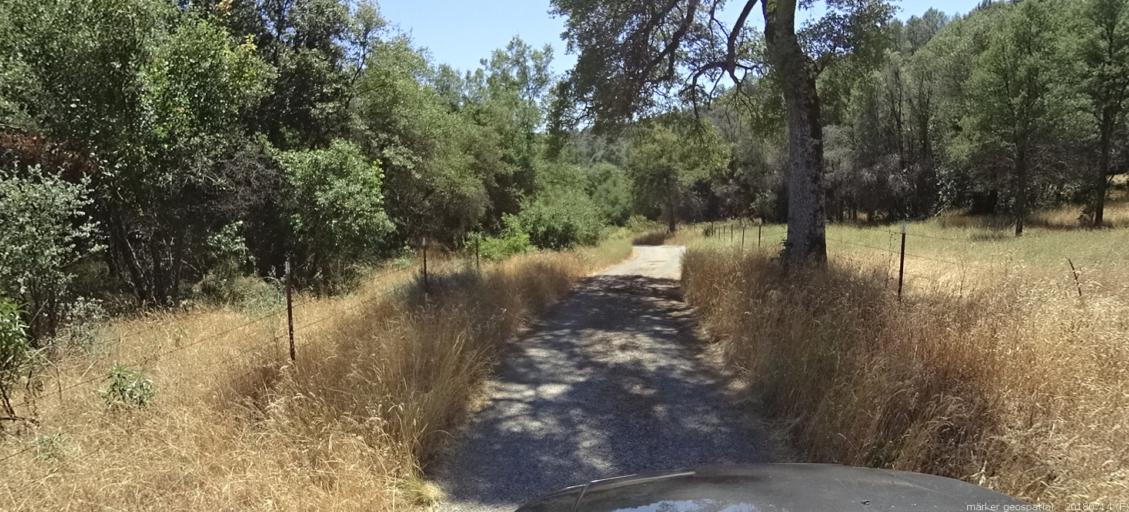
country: US
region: California
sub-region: Madera County
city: Ahwahnee
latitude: 37.3859
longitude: -119.7598
